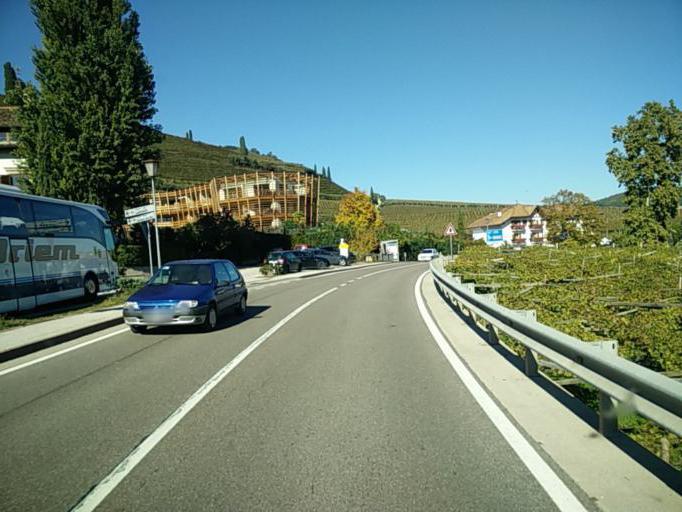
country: IT
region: Trentino-Alto Adige
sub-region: Bolzano
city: Caldaro sulla Strada del Vino
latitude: 46.3848
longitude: 11.2538
